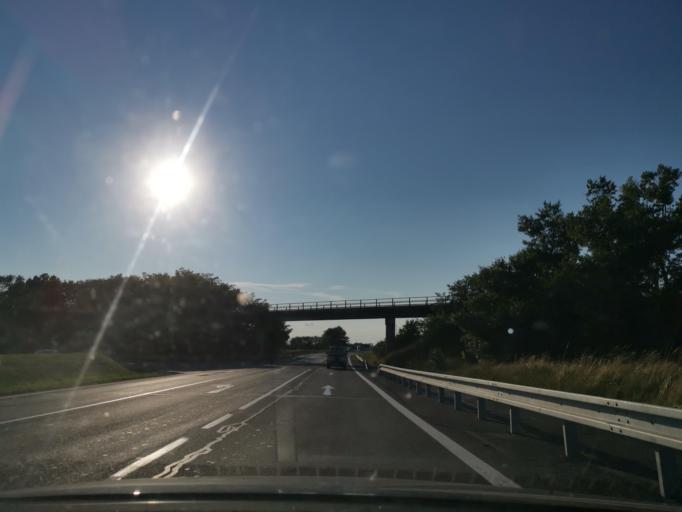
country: SK
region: Bratislavsky
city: Stupava
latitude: 48.3281
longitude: 17.0201
